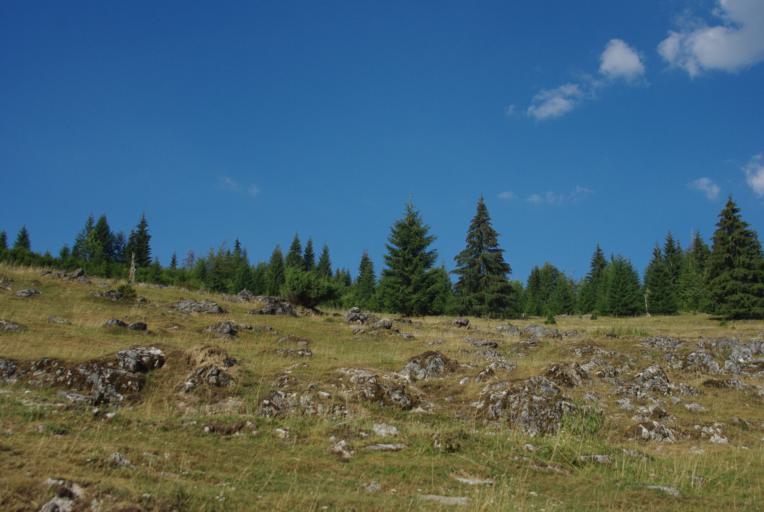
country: RO
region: Alba
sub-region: Comuna Arieseni
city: Arieseni
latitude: 46.5861
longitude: 22.6976
